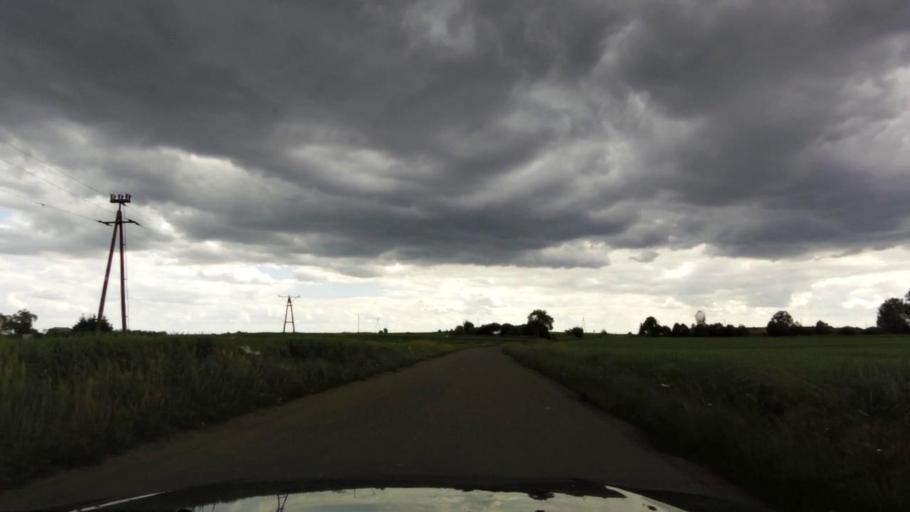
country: PL
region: West Pomeranian Voivodeship
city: Trzcinsko Zdroj
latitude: 52.9586
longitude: 14.6097
